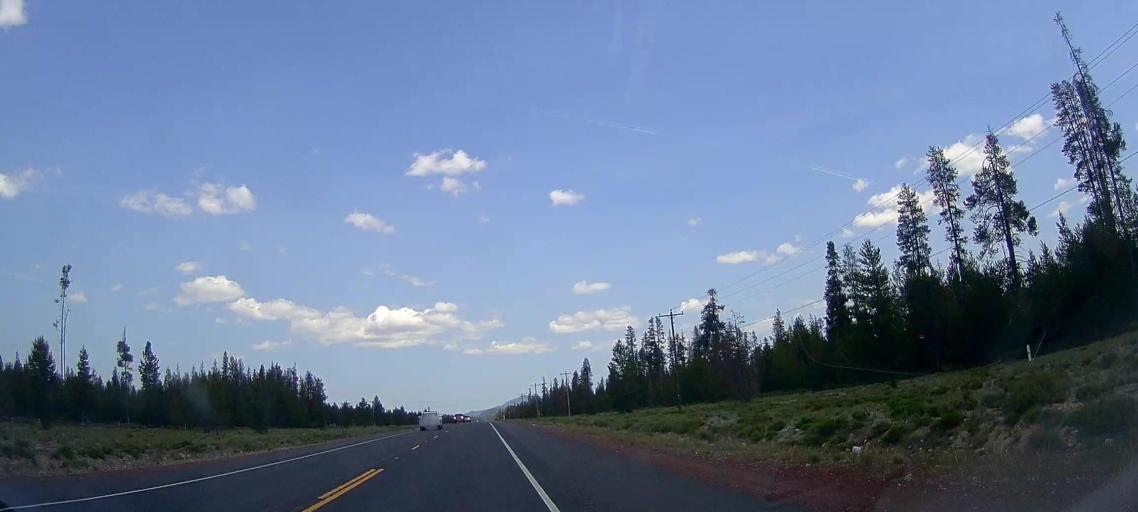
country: US
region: Oregon
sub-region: Deschutes County
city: La Pine
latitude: 43.1441
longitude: -121.7990
